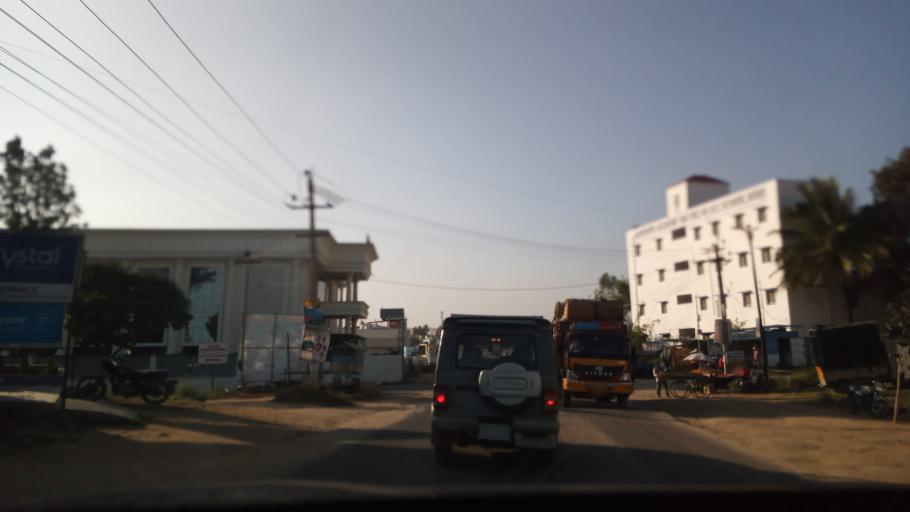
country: IN
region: Tamil Nadu
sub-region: Krishnagiri
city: Hosur
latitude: 12.7186
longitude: 77.8329
